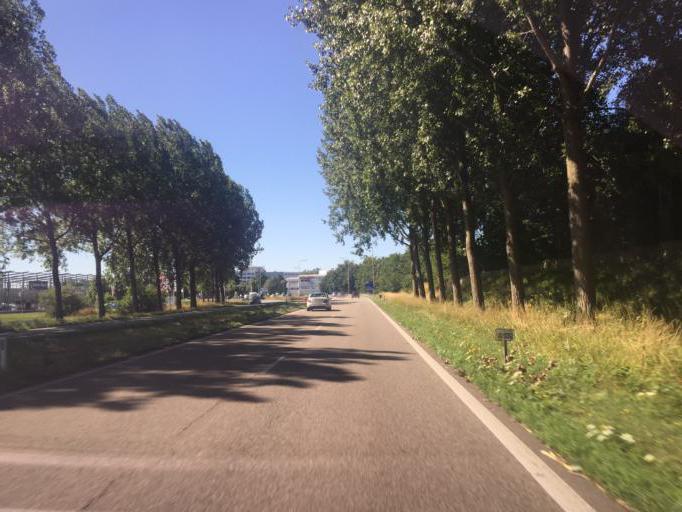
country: NL
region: North Holland
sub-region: Gemeente Haarlemmermeer
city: Hoofddorp
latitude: 52.2999
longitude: 4.7105
